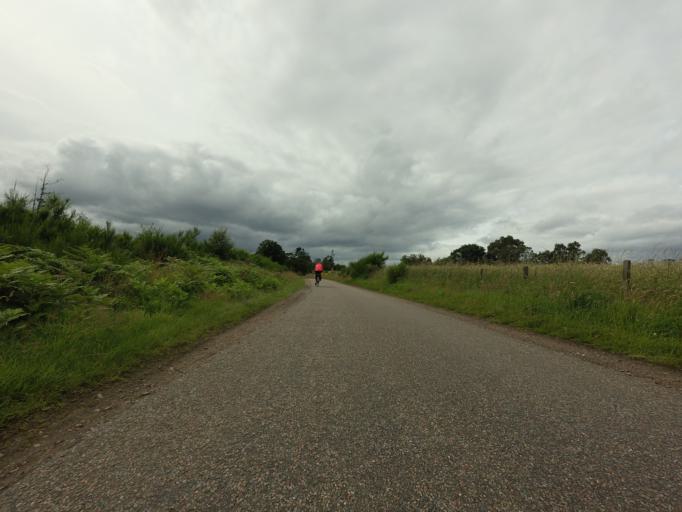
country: GB
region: Scotland
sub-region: Moray
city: Forres
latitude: 57.6049
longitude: -3.7499
